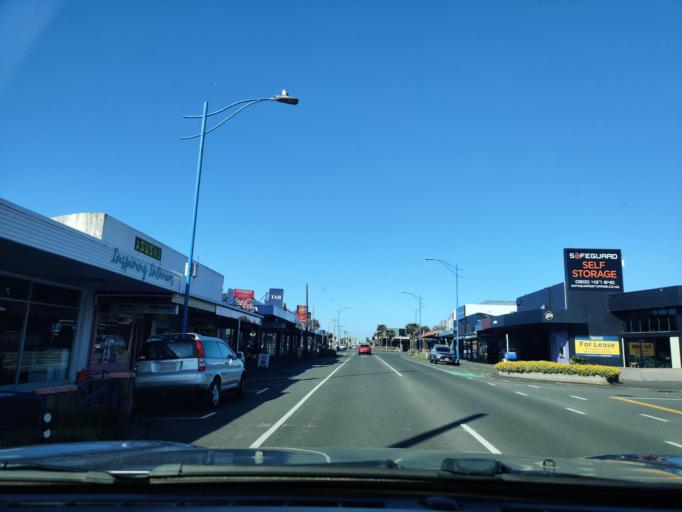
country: NZ
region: Taranaki
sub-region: New Plymouth District
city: New Plymouth
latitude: -39.0496
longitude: 174.1011
